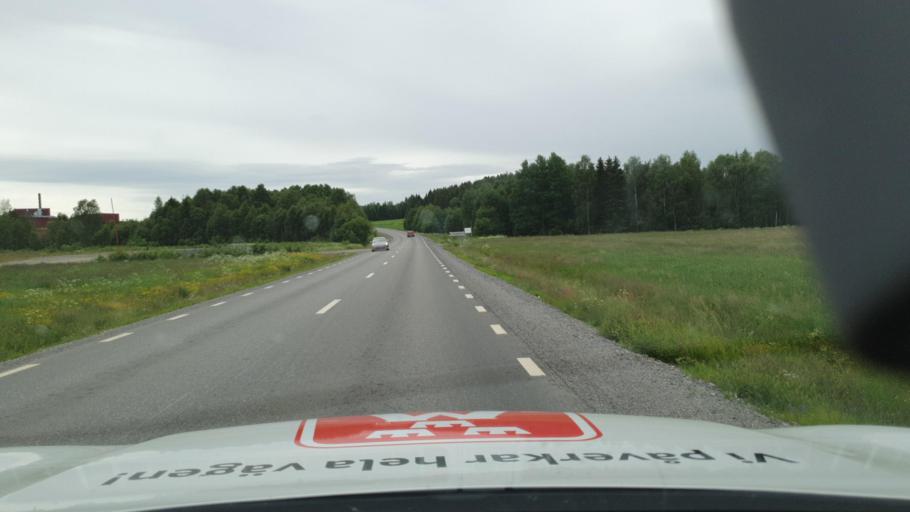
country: SE
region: Vaesterbotten
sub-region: Skelleftea Kommun
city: Burtraesk
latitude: 64.3689
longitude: 20.5023
